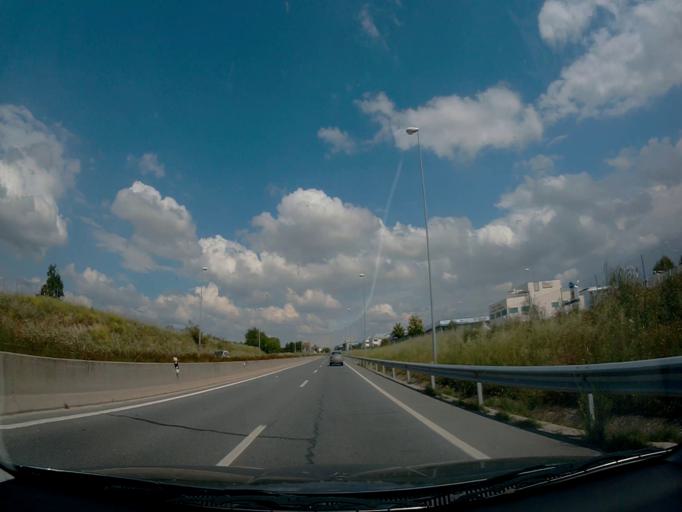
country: ES
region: Madrid
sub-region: Provincia de Madrid
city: Villaviciosa de Odon
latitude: 40.3511
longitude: -3.8978
